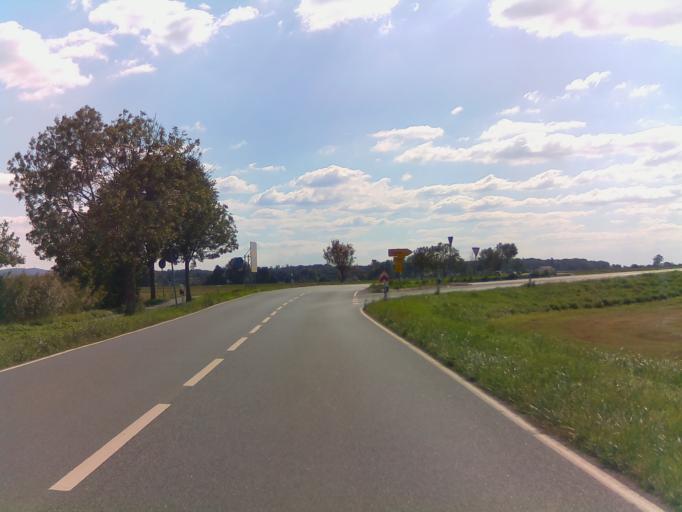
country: DE
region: Hesse
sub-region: Regierungsbezirk Darmstadt
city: Alsbach-Hahnlein
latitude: 49.7311
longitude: 8.5732
